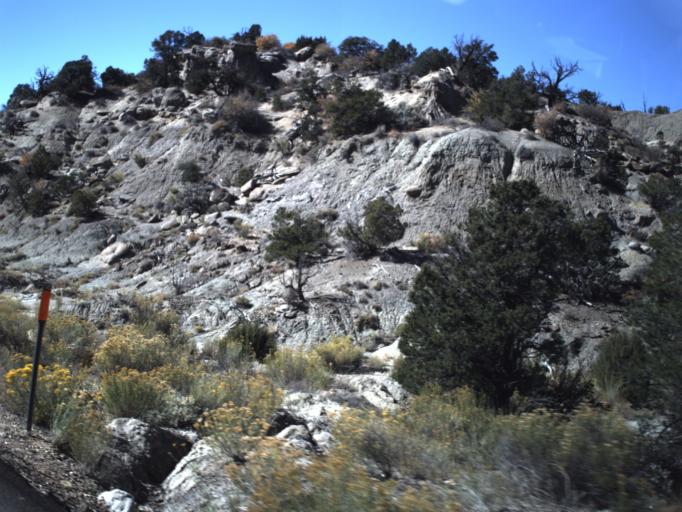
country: US
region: Utah
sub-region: Garfield County
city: Panguitch
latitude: 37.6232
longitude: -111.8564
